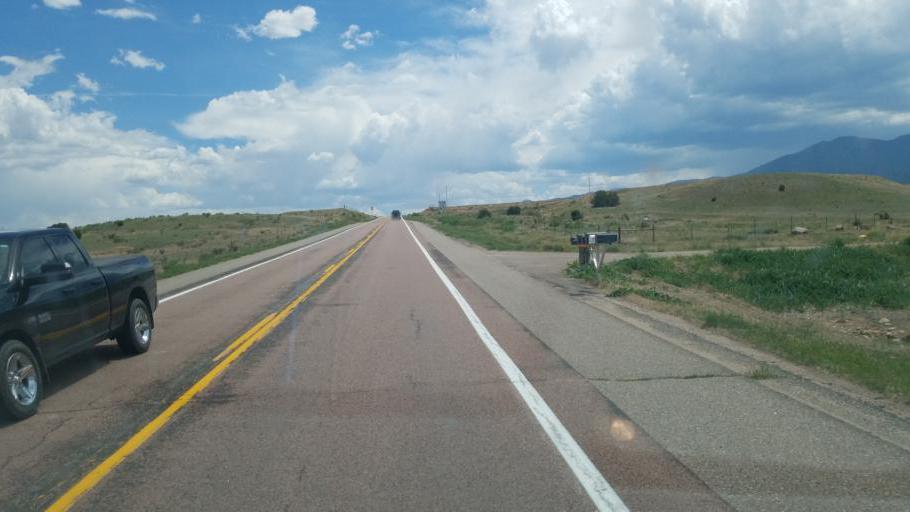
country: US
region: Colorado
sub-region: Fremont County
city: Florence
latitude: 38.2947
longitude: -105.0878
